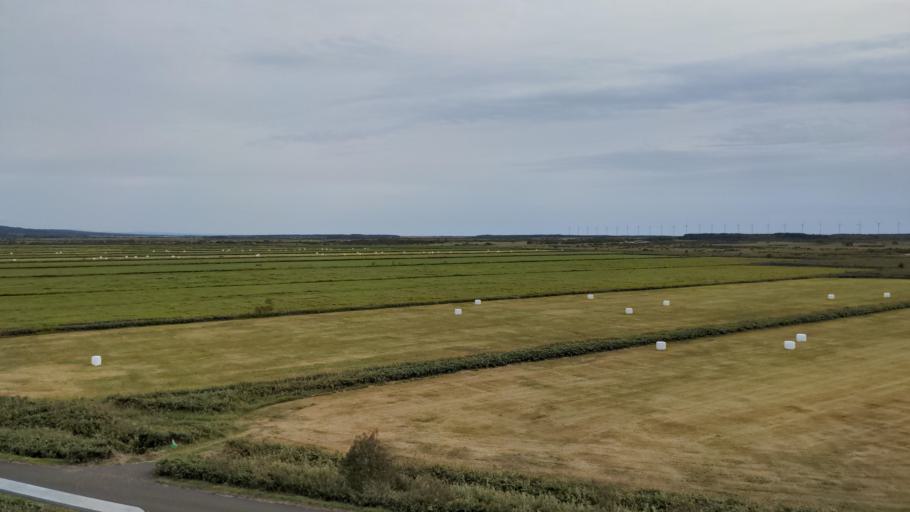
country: JP
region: Hokkaido
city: Makubetsu
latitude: 45.0094
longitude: 141.7322
